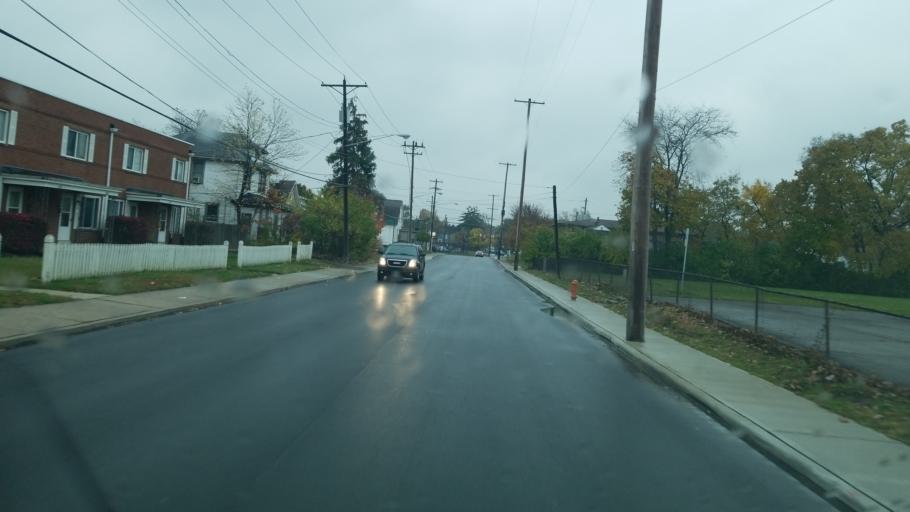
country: US
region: Ohio
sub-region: Franklin County
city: Grandview Heights
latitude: 39.9901
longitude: -83.0354
